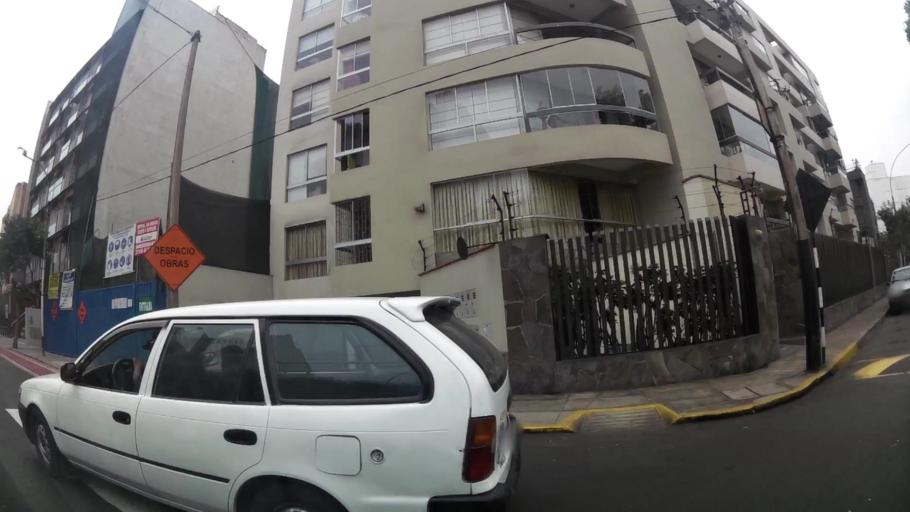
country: PE
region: Lima
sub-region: Lima
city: San Isidro
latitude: -12.1229
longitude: -77.0358
